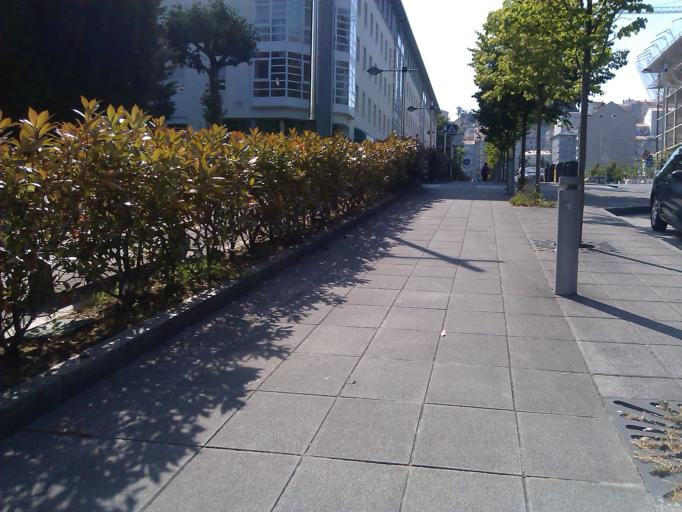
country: ES
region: Galicia
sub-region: Provincia da Coruna
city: Santiago de Compostela
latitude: 42.8835
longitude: -8.5306
